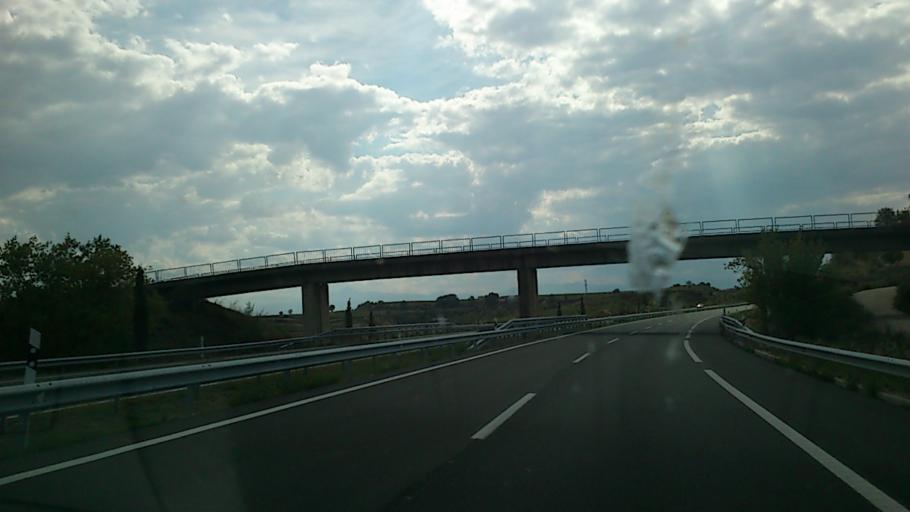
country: ES
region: La Rioja
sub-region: Provincia de La Rioja
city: Haro
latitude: 42.5962
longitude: -2.8585
